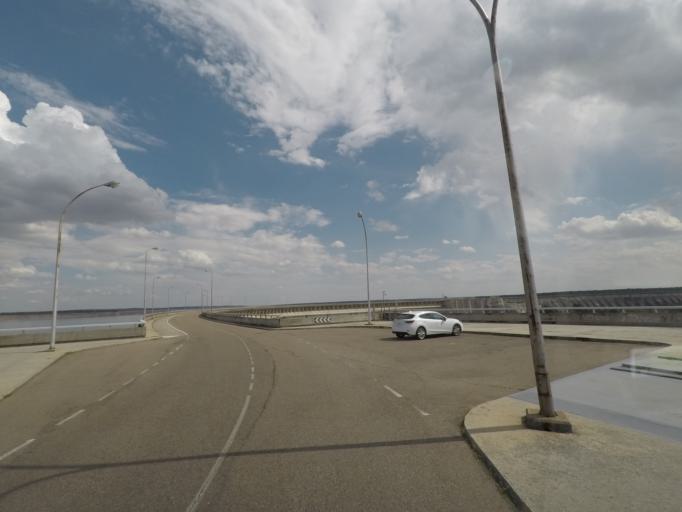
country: ES
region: Castille and Leon
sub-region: Provincia de Salamanca
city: Almendra
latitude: 41.2733
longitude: -6.3233
